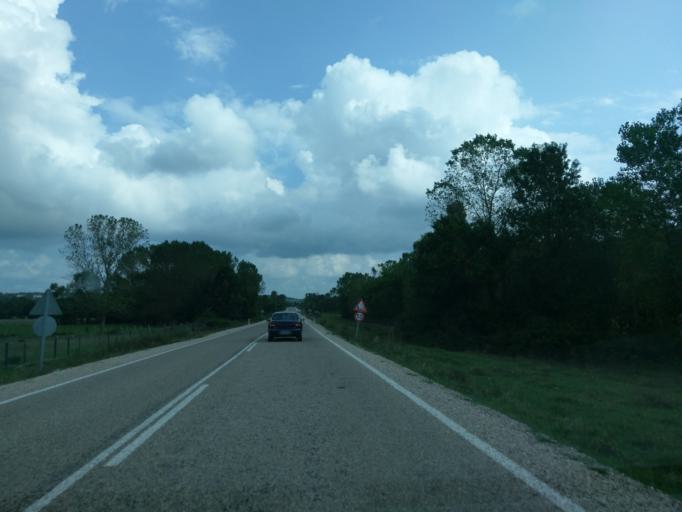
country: TR
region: Sinop
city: Erfelek
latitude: 42.0215
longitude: 34.9851
